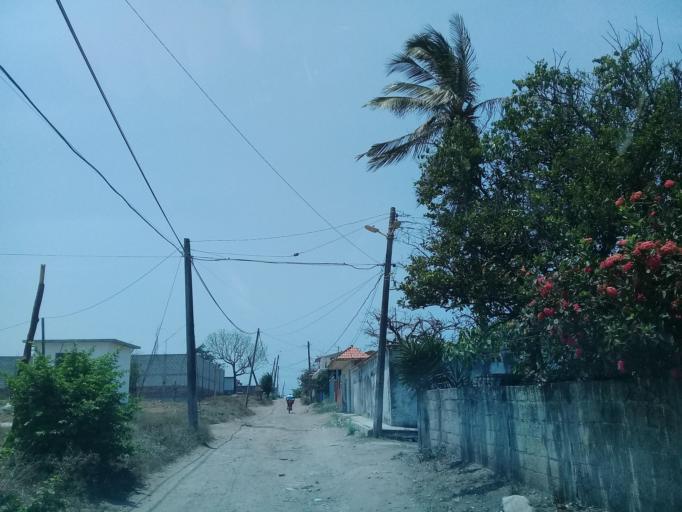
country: MX
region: Veracruz
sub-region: Veracruz
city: Las Amapolas
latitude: 19.1590
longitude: -96.2139
